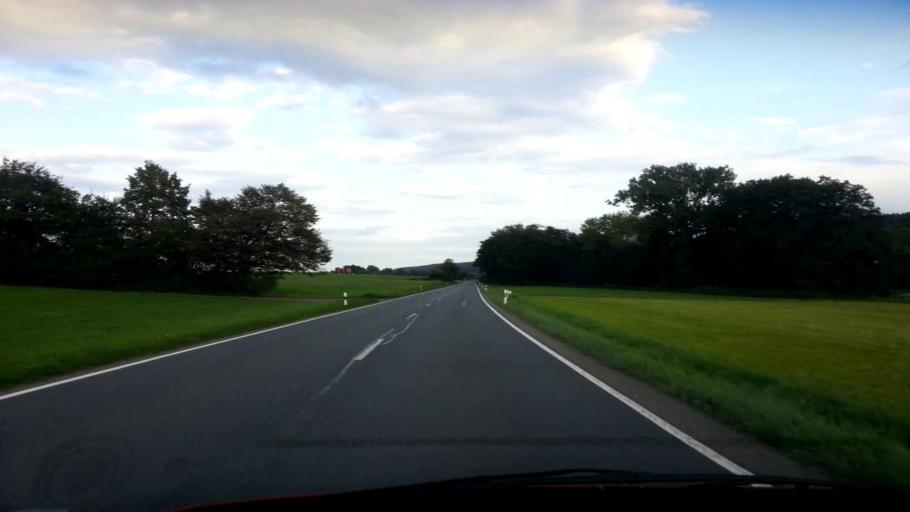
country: DE
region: Bavaria
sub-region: Regierungsbezirk Unterfranken
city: Geiselwind
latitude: 49.7721
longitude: 10.4865
